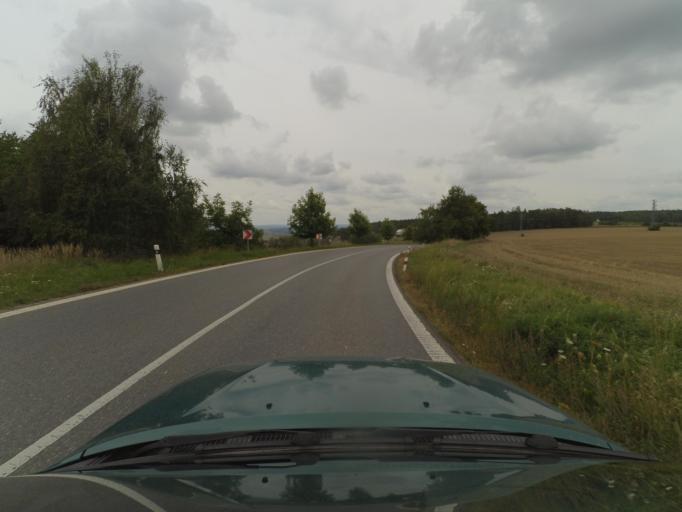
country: CZ
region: Plzensky
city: Kozlany
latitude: 50.0518
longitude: 13.6242
